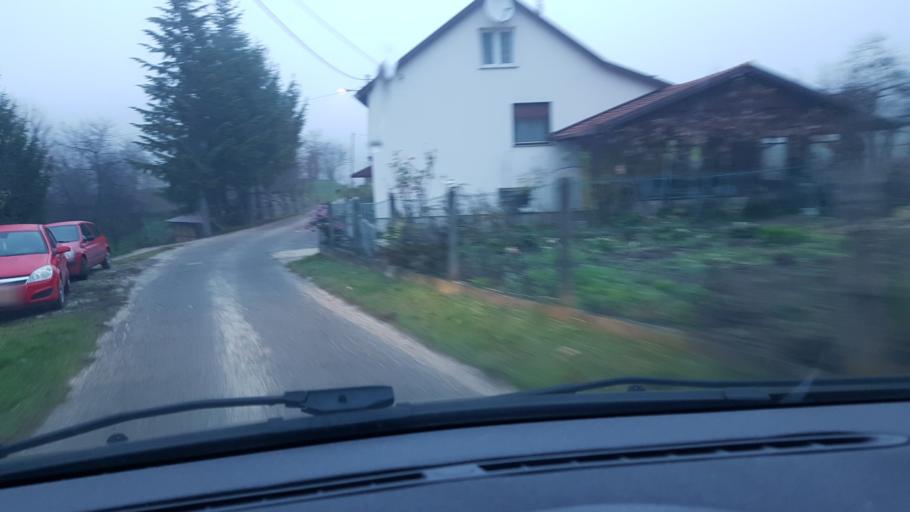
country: HR
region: Krapinsko-Zagorska
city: Pregrada
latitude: 46.1930
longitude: 15.7418
